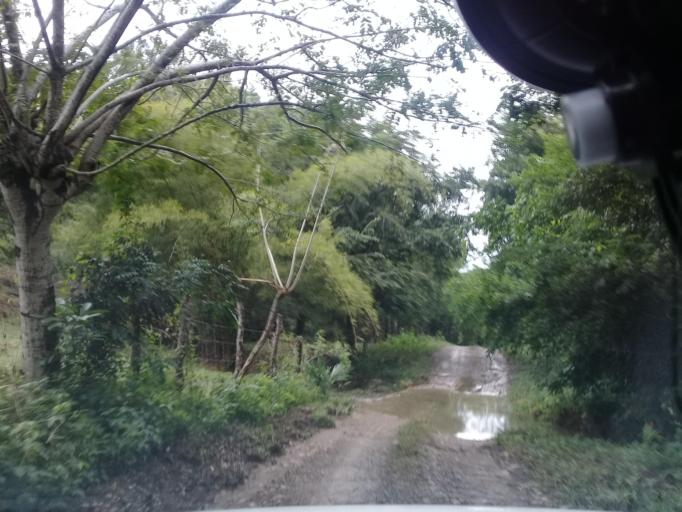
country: MX
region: Veracruz
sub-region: Chalma
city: San Pedro Coyutla
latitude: 21.2379
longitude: -98.4330
